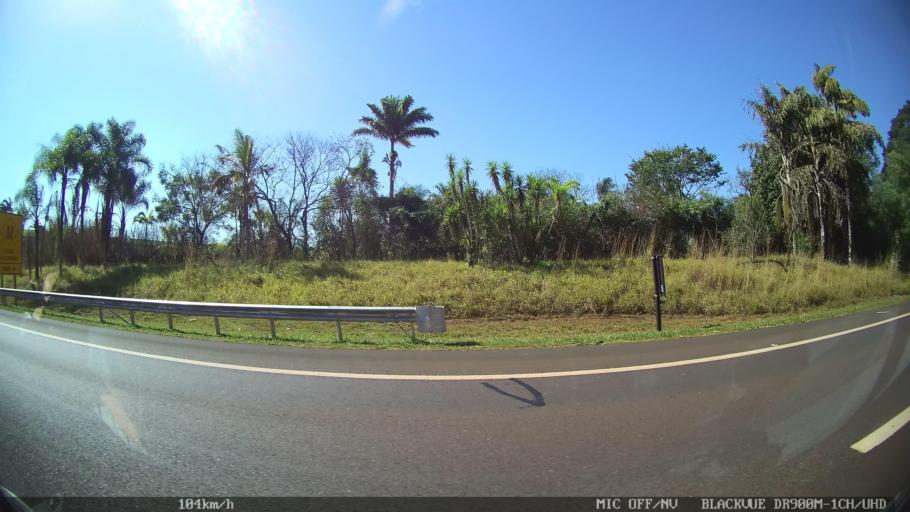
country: BR
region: Sao Paulo
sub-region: Batatais
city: Batatais
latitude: -20.8473
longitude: -47.6013
